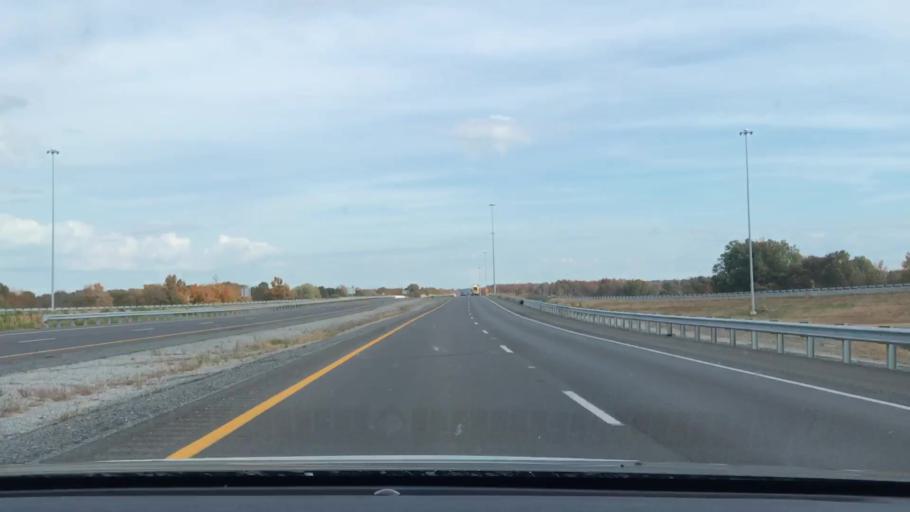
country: US
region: Kentucky
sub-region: Marshall County
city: Benton
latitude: 36.8688
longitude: -88.3661
